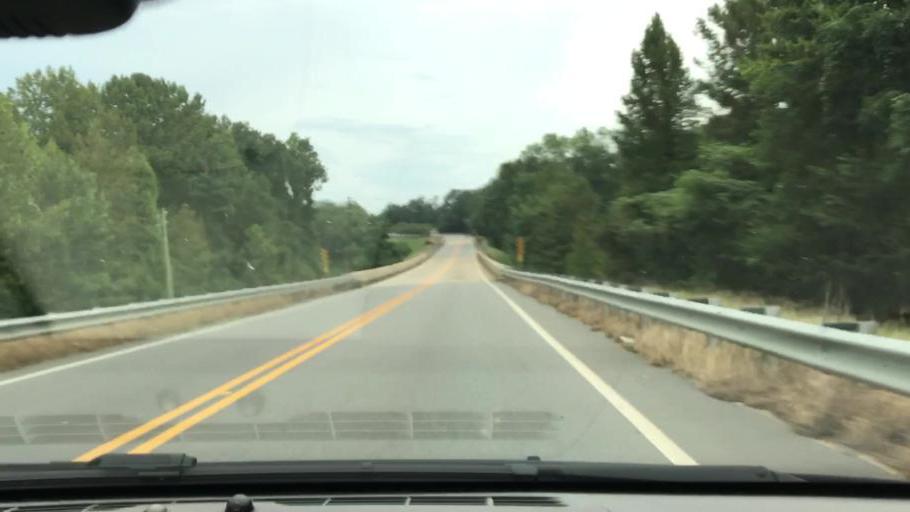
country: US
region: Alabama
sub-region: Houston County
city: Ashford
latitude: 31.2886
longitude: -85.1028
